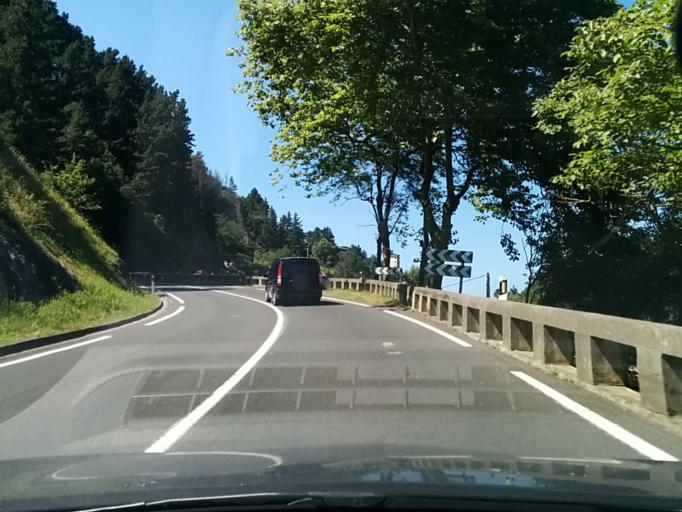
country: ES
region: Basque Country
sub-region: Bizkaia
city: Ondarroa
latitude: 43.3164
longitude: -2.4116
